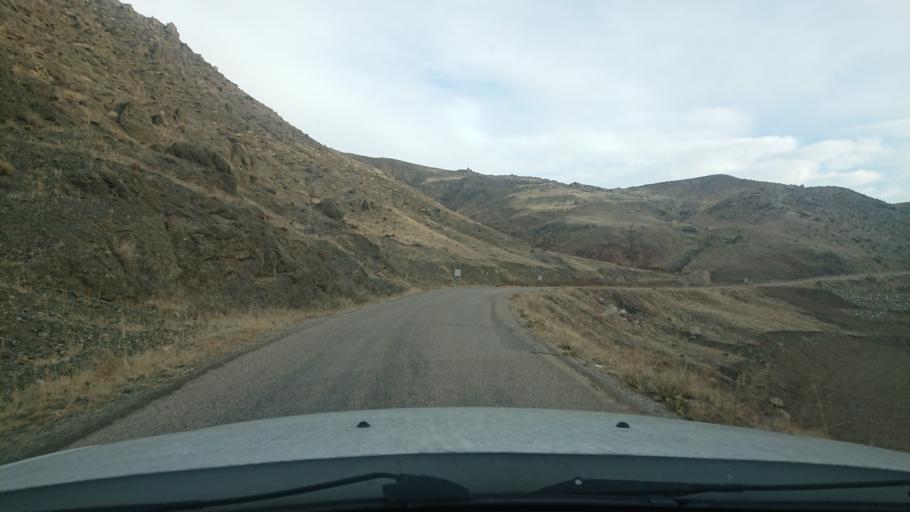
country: TR
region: Aksaray
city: Acipinar
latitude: 38.6207
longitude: 33.7882
